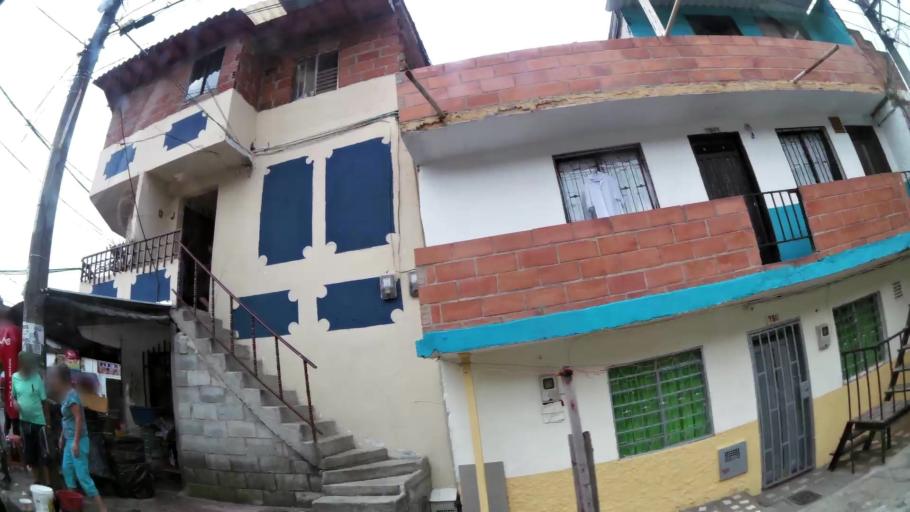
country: CO
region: Antioquia
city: Medellin
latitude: 6.2916
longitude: -75.5612
